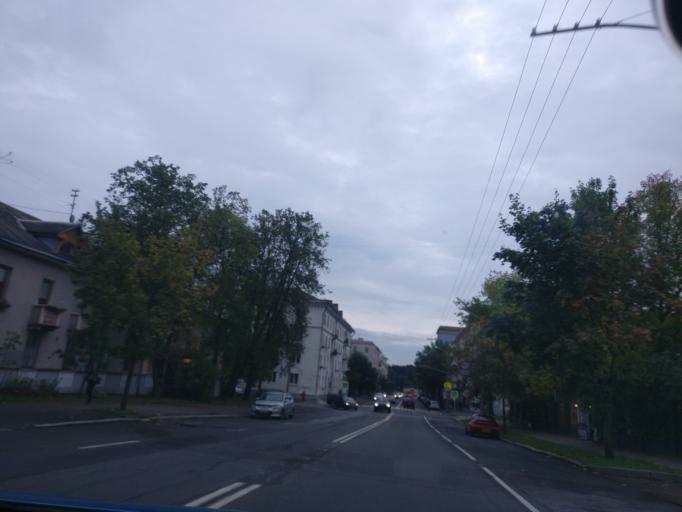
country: BY
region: Minsk
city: Minsk
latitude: 53.9262
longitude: 27.6068
